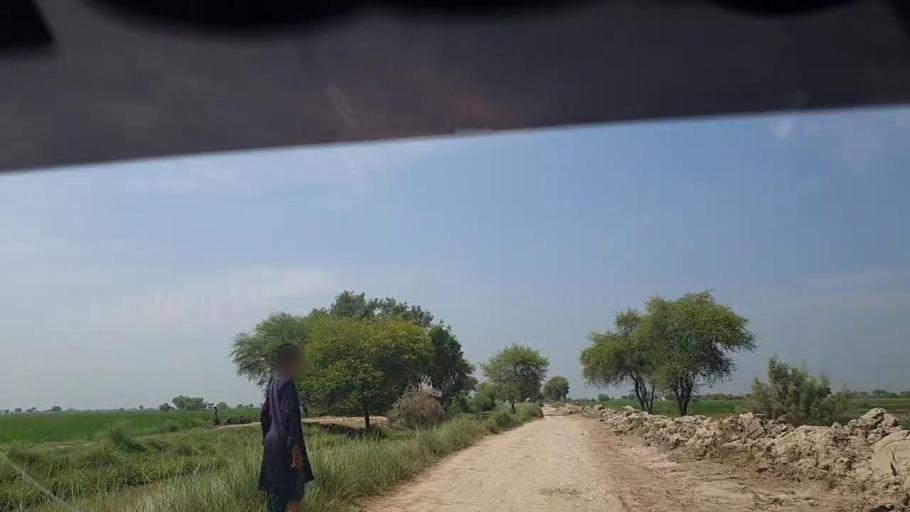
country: PK
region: Sindh
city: Thul
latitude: 28.1840
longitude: 68.7222
